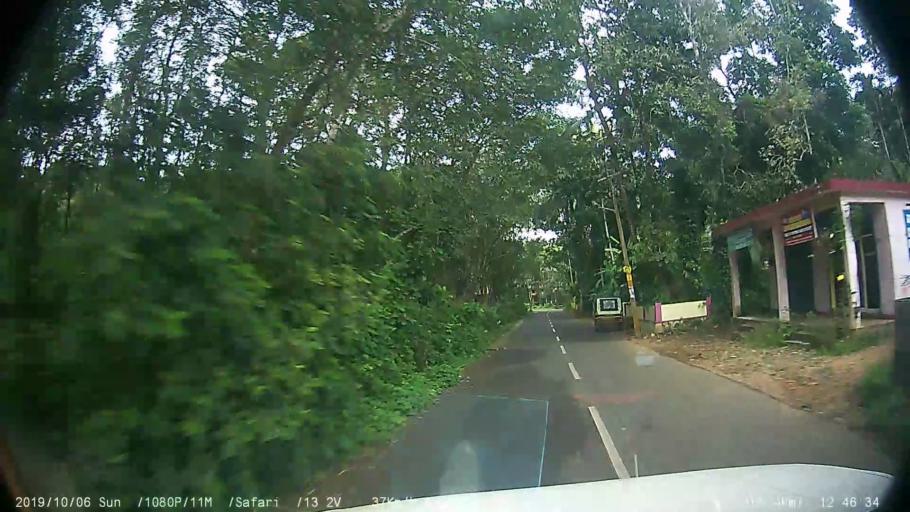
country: IN
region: Kerala
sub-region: Kottayam
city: Palackattumala
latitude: 9.7715
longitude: 76.6066
